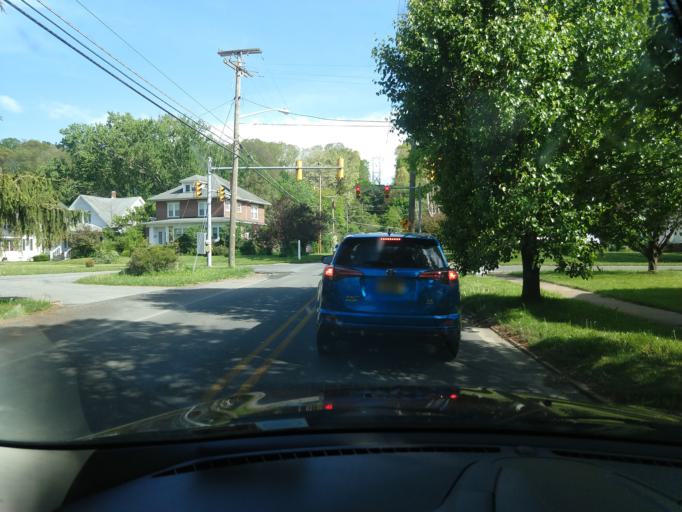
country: US
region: West Virginia
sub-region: Mercer County
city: Bluefield
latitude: 37.2511
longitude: -81.2317
